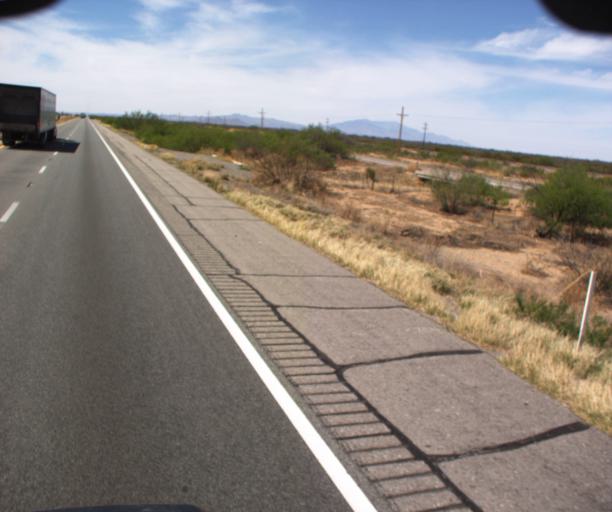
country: US
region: Arizona
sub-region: Cochise County
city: Willcox
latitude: 32.3019
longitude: -109.3732
